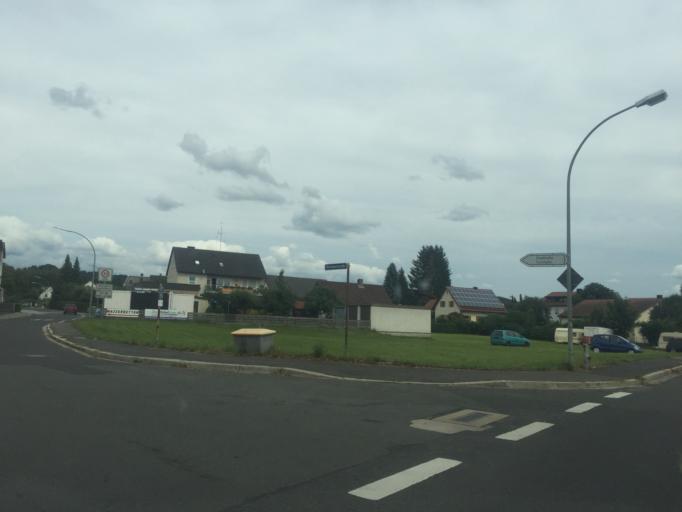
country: DE
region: Bavaria
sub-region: Upper Palatinate
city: Pressath
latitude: 49.7647
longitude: 11.9384
